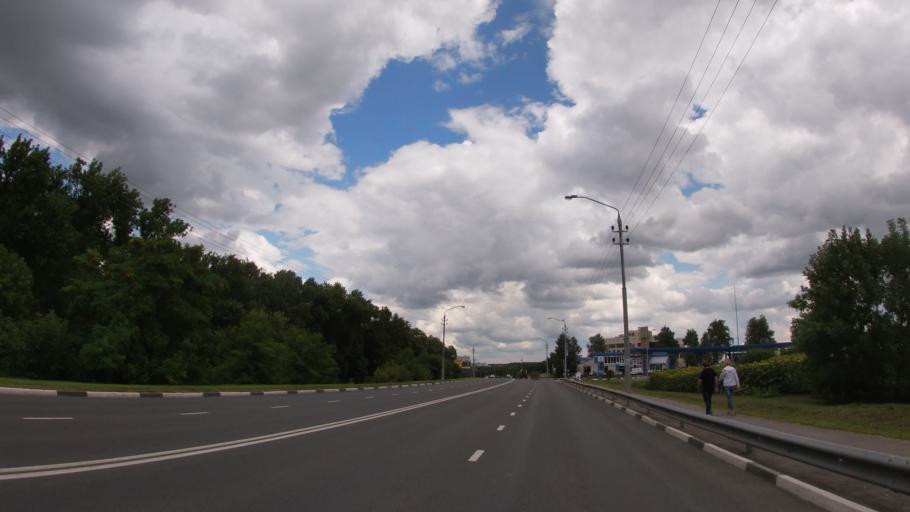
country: RU
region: Belgorod
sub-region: Belgorodskiy Rayon
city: Belgorod
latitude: 50.5530
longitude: 36.5792
